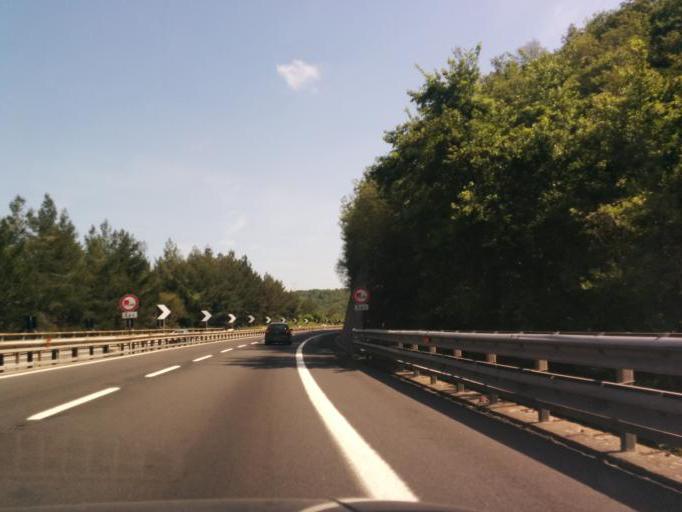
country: IT
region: Tuscany
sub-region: Province of Florence
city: Carraia
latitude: 43.9318
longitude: 11.2194
